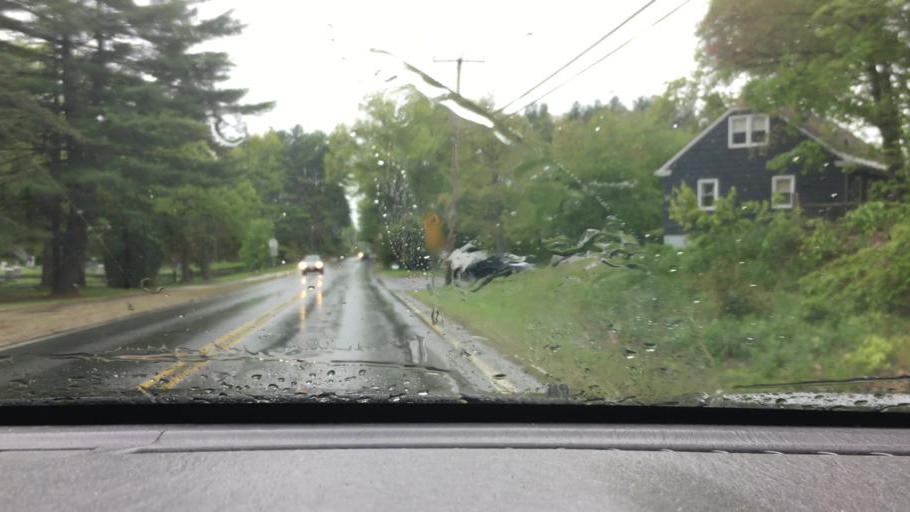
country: US
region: Massachusetts
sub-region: Franklin County
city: Turners Falls
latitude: 42.5887
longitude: -72.5521
